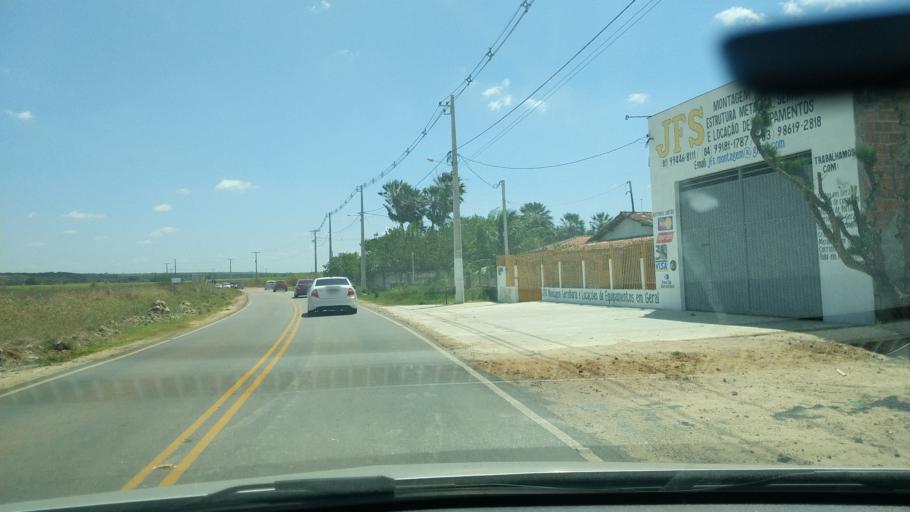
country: BR
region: Rio Grande do Norte
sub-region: Goianinha
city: Goianinha
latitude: -6.2485
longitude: -35.1848
